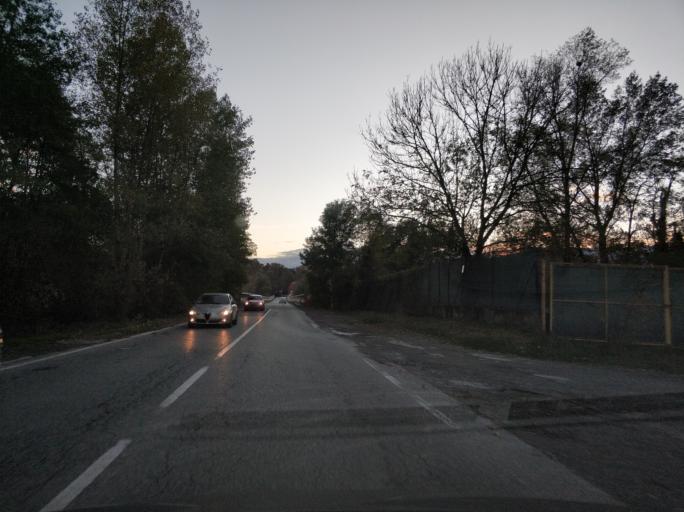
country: IT
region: Piedmont
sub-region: Provincia di Torino
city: Robassomero
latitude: 45.2059
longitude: 7.5746
